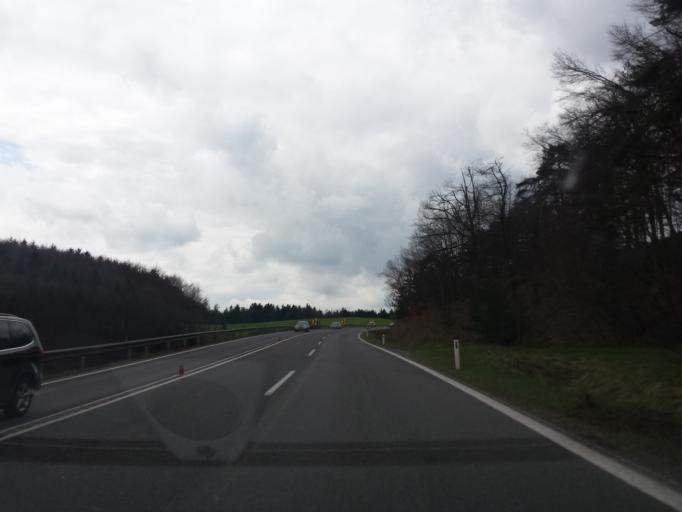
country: AT
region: Lower Austria
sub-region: Politischer Bezirk Krems
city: Lengenfeld
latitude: 48.5024
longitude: 15.5391
